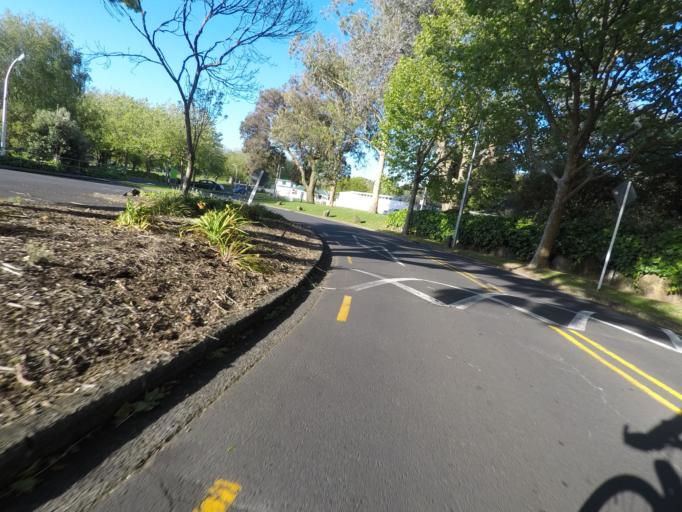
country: NZ
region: Auckland
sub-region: Auckland
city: Rosebank
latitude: -36.8818
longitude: 174.7096
